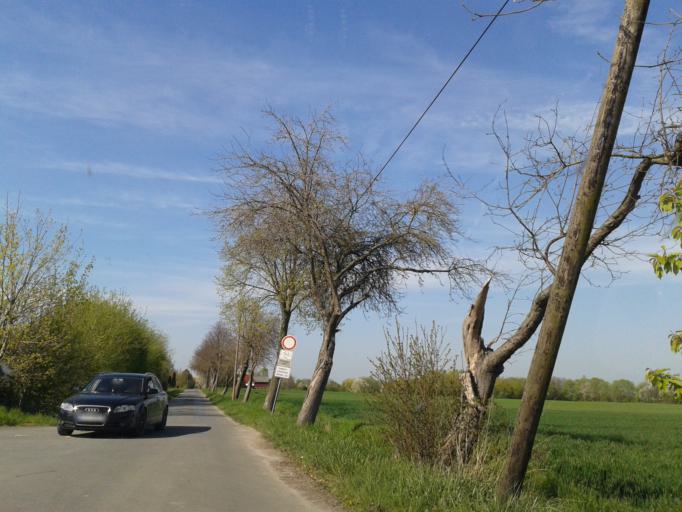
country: DE
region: North Rhine-Westphalia
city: Geseke
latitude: 51.6504
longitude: 8.5057
